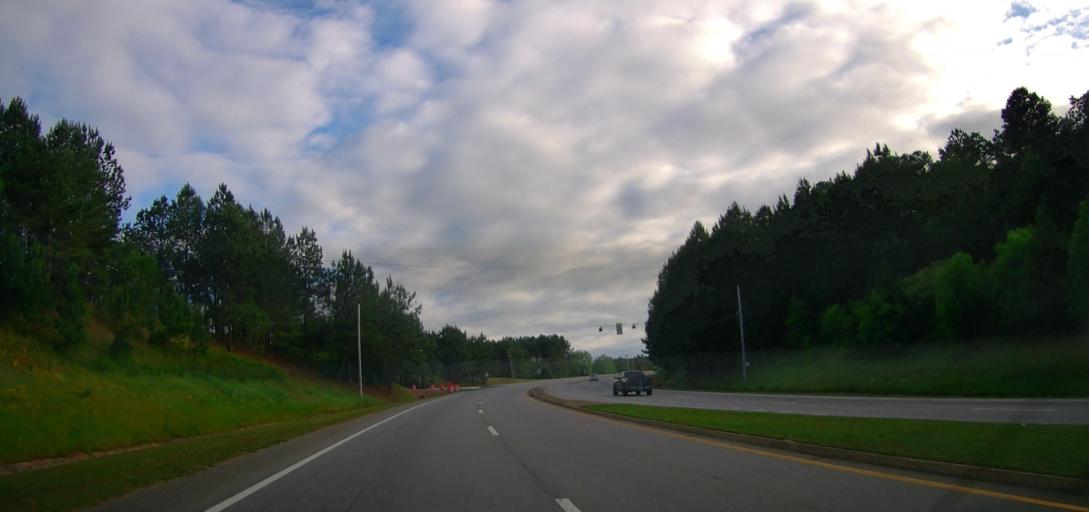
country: US
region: Georgia
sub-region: Oconee County
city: Watkinsville
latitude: 33.9057
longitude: -83.4041
